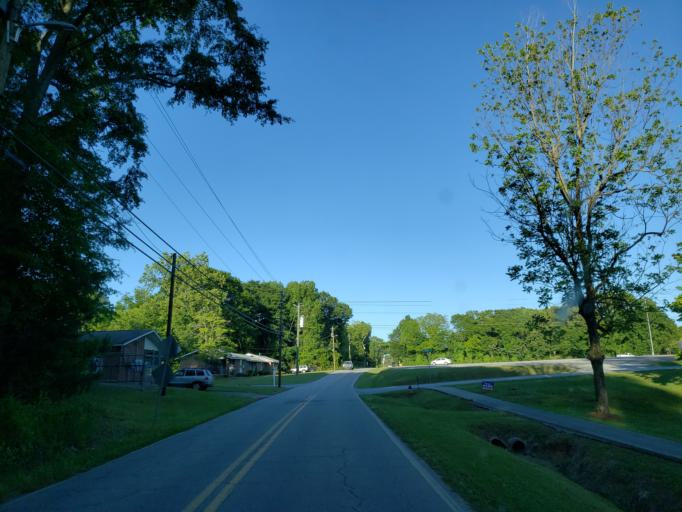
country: US
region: Georgia
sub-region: Haralson County
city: Tallapoosa
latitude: 33.7545
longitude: -85.2978
